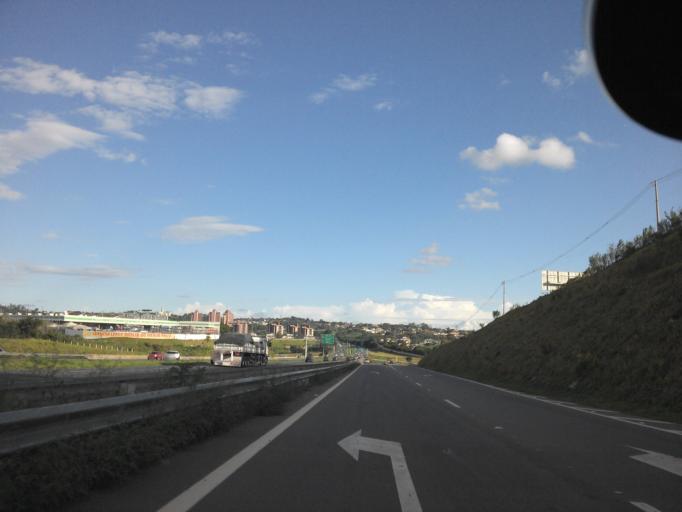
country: BR
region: Sao Paulo
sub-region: Campinas
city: Campinas
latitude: -22.8807
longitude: -47.0149
